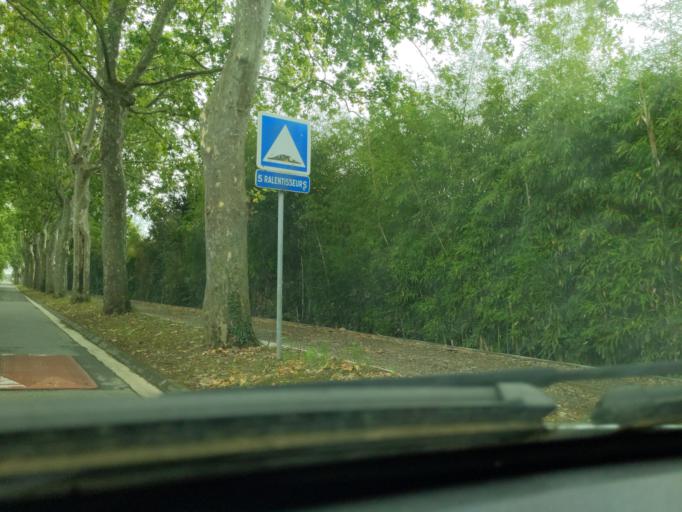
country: FR
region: Midi-Pyrenees
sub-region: Departement de la Haute-Garonne
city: Tournefeuille
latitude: 43.5780
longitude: 1.3607
